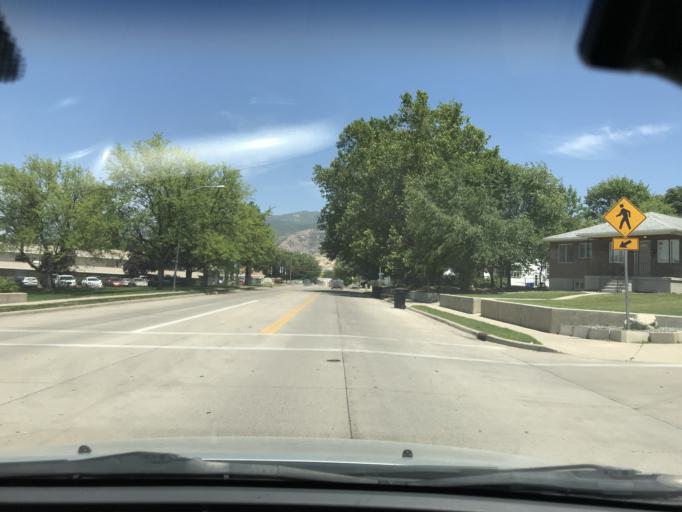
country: US
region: Utah
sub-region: Davis County
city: Woods Cross
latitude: 40.8767
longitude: -111.8840
